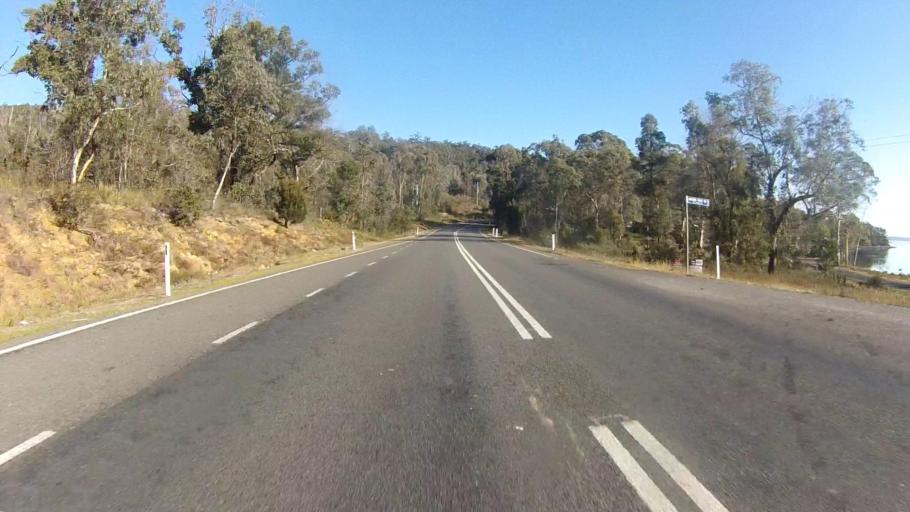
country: AU
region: Tasmania
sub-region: Clarence
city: Sandford
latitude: -43.0246
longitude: 147.8836
